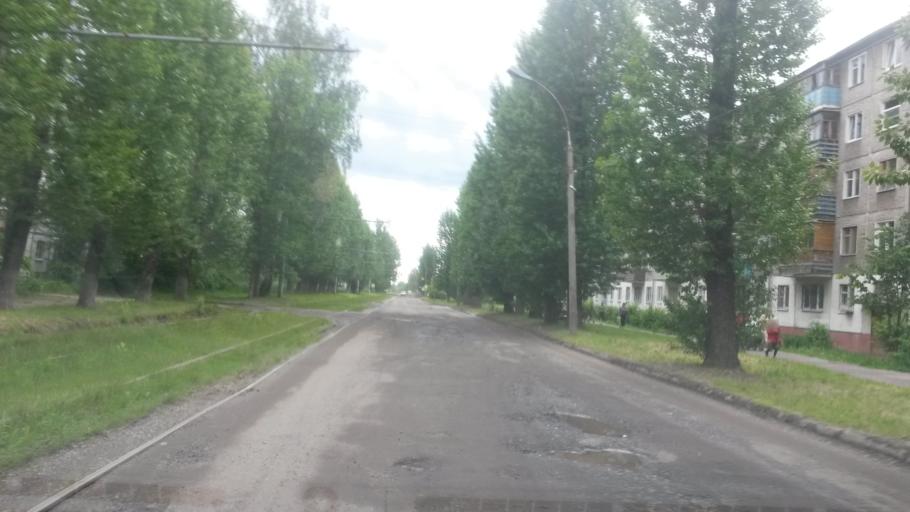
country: RU
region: Jaroslavl
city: Yaroslavl
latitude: 57.6859
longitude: 39.8062
